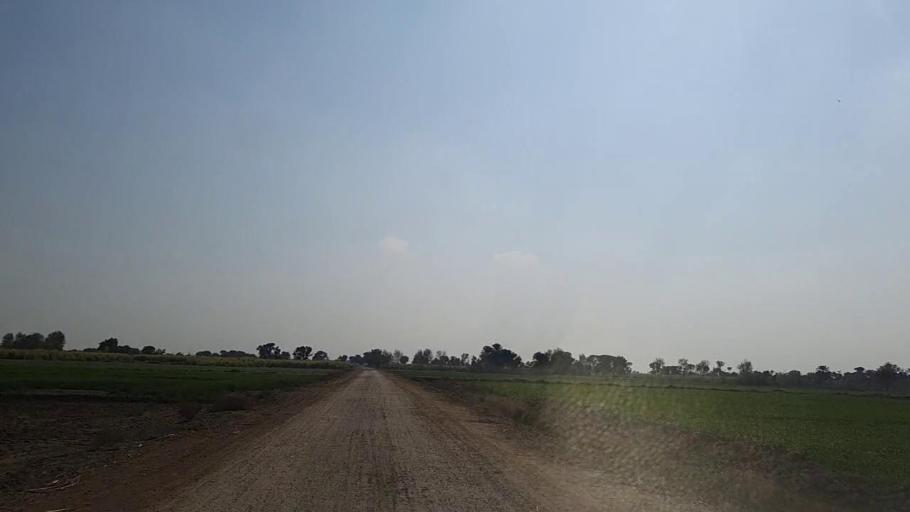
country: PK
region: Sindh
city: Daur
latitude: 26.4406
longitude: 68.2332
